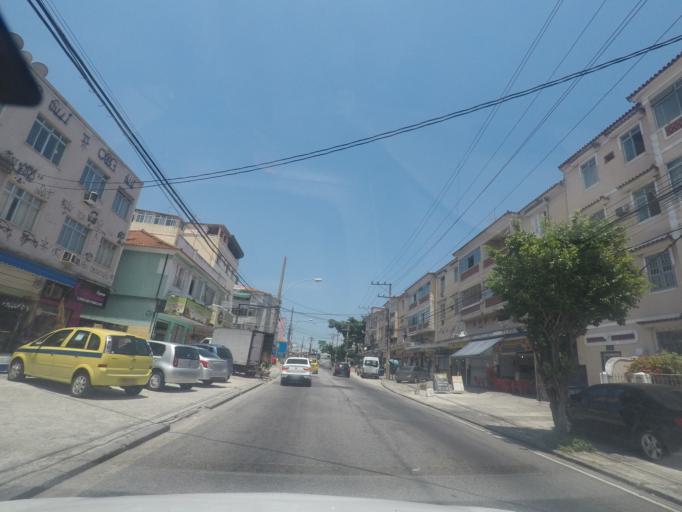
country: BR
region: Rio de Janeiro
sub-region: Duque De Caxias
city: Duque de Caxias
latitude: -22.8396
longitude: -43.2975
